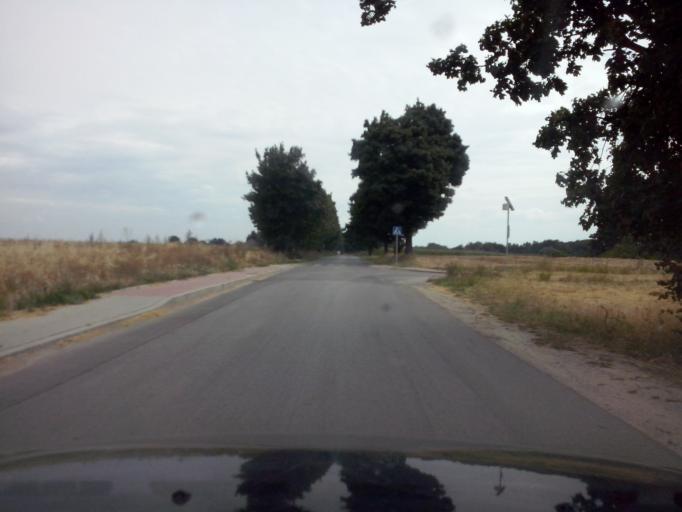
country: PL
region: Swietokrzyskie
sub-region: Powiat kielecki
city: Lagow
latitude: 50.7300
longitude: 21.1054
